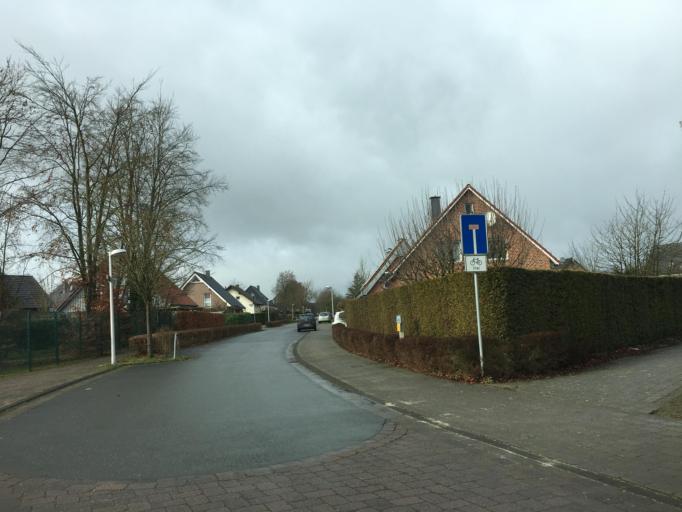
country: DE
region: North Rhine-Westphalia
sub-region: Regierungsbezirk Munster
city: Senden
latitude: 51.9207
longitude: 7.4703
